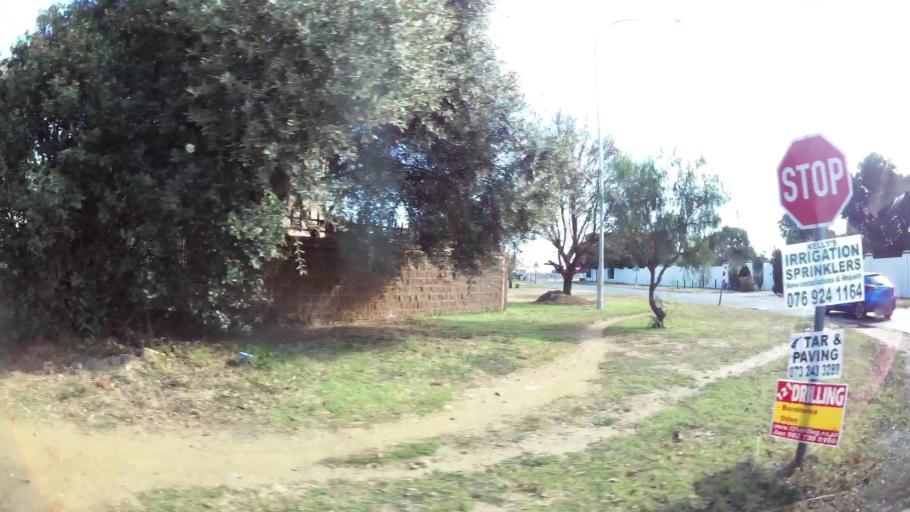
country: ZA
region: Gauteng
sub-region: Ekurhuleni Metropolitan Municipality
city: Benoni
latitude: -26.1301
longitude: 28.3424
